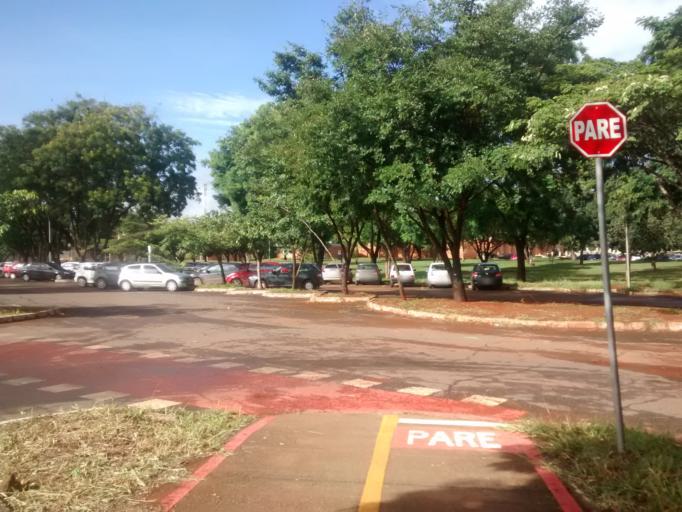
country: BR
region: Federal District
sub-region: Brasilia
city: Brasilia
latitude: -15.7617
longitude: -47.8728
